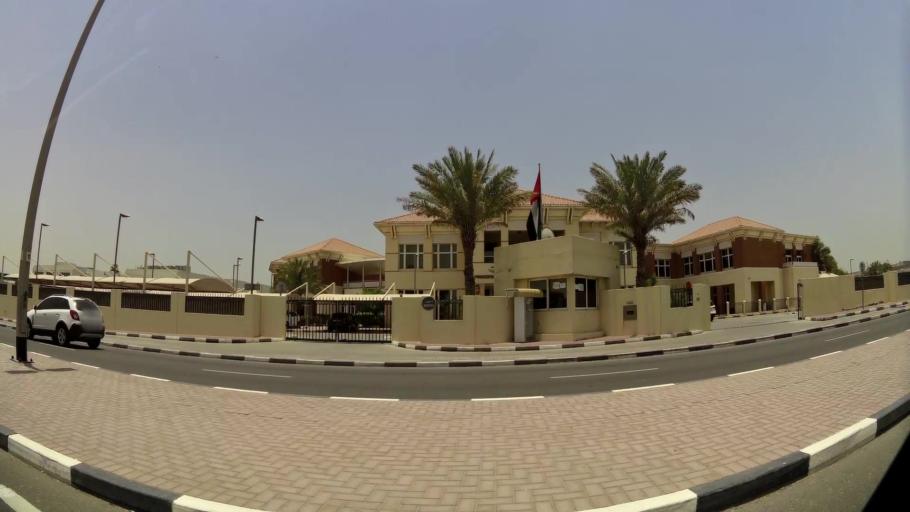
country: AE
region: Ash Shariqah
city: Sharjah
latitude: 25.2277
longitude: 55.3873
